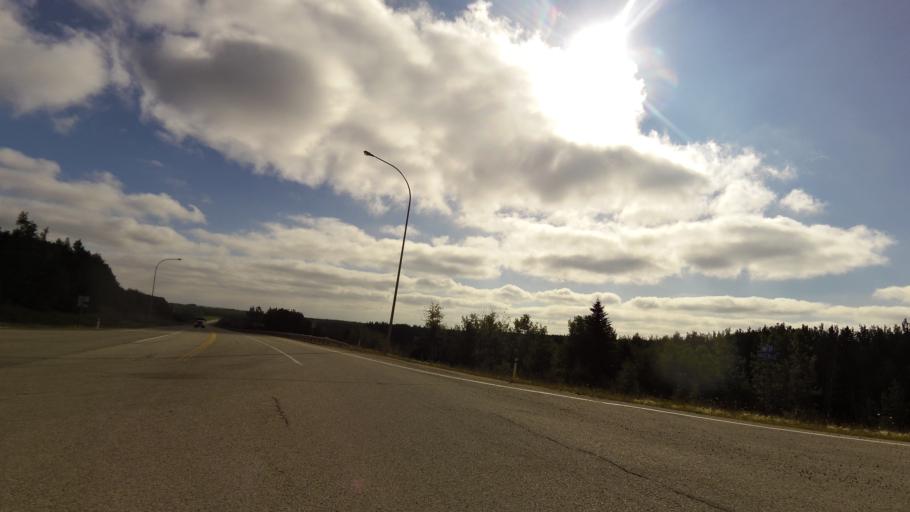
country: CA
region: Alberta
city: Drayton Valley
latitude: 53.2079
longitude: -114.7817
